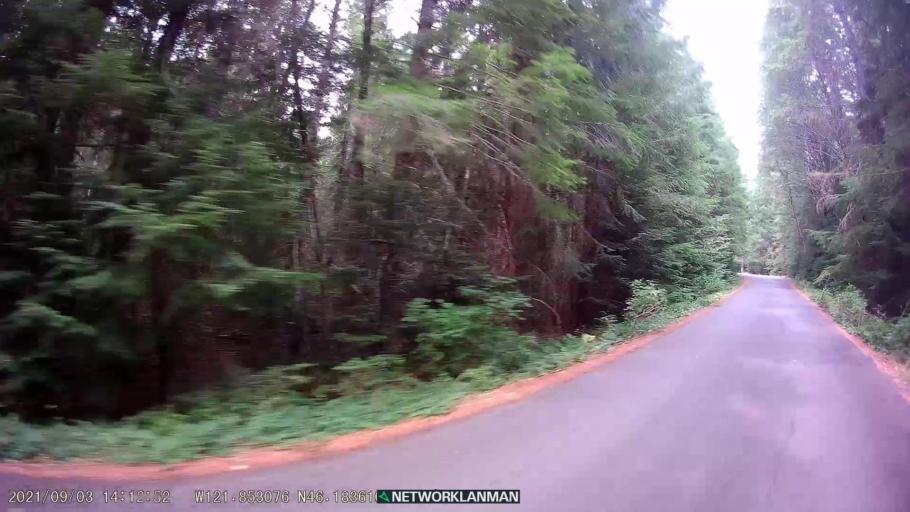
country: US
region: Washington
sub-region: Skamania County
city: Carson
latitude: 46.1838
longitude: -121.8530
